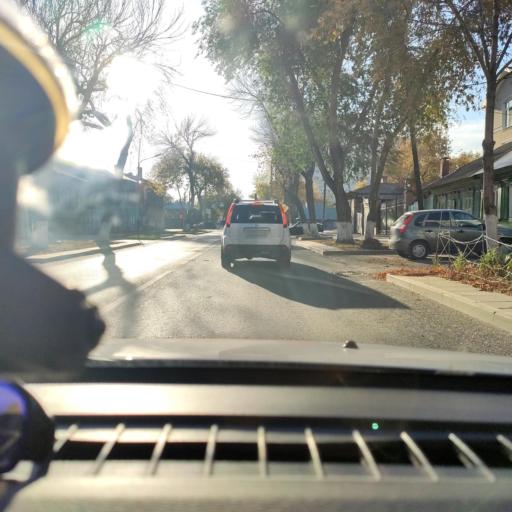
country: RU
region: Samara
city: Samara
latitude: 53.1990
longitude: 50.1206
